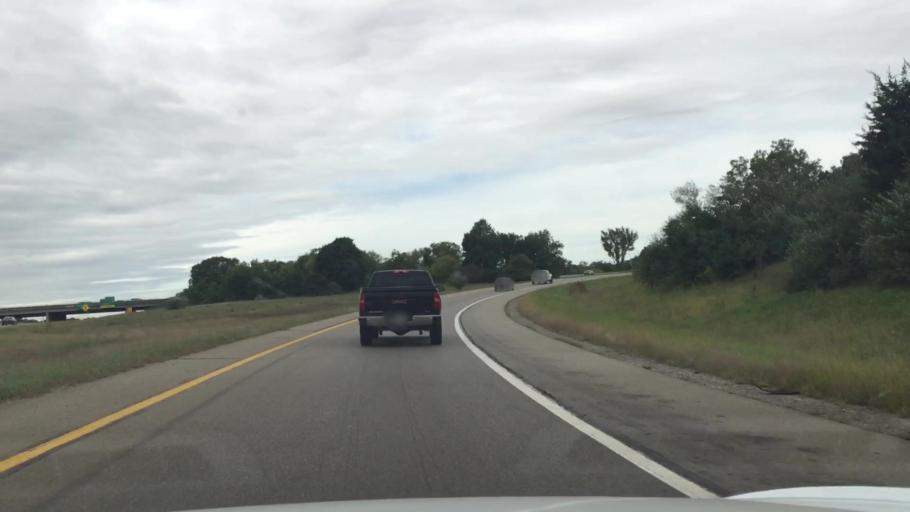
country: US
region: Michigan
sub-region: Oakland County
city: Auburn Hills
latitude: 42.6420
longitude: -83.2342
